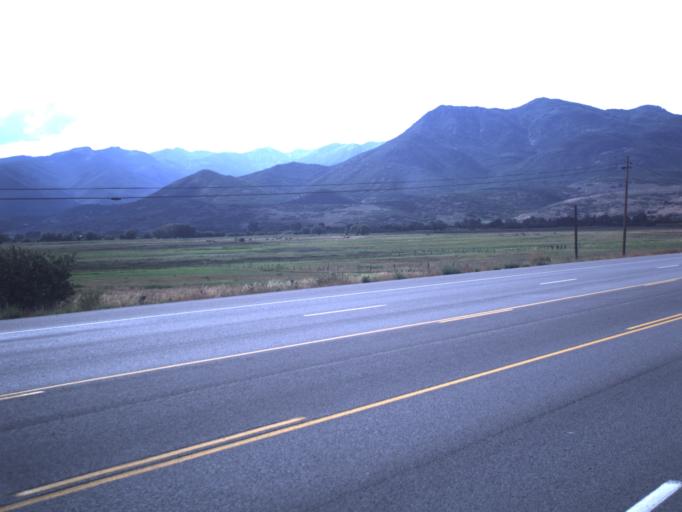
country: US
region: Utah
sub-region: Wasatch County
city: Heber
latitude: 40.5370
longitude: -111.4113
